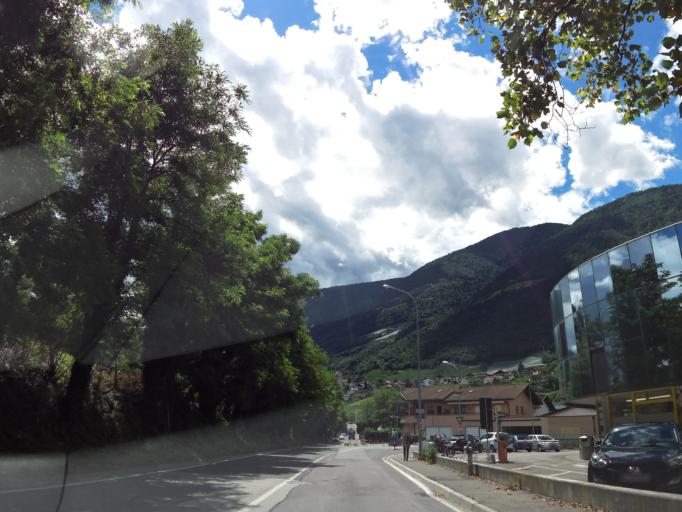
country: IT
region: Trentino-Alto Adige
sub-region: Bolzano
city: Marlengo
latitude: 46.6614
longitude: 11.1491
